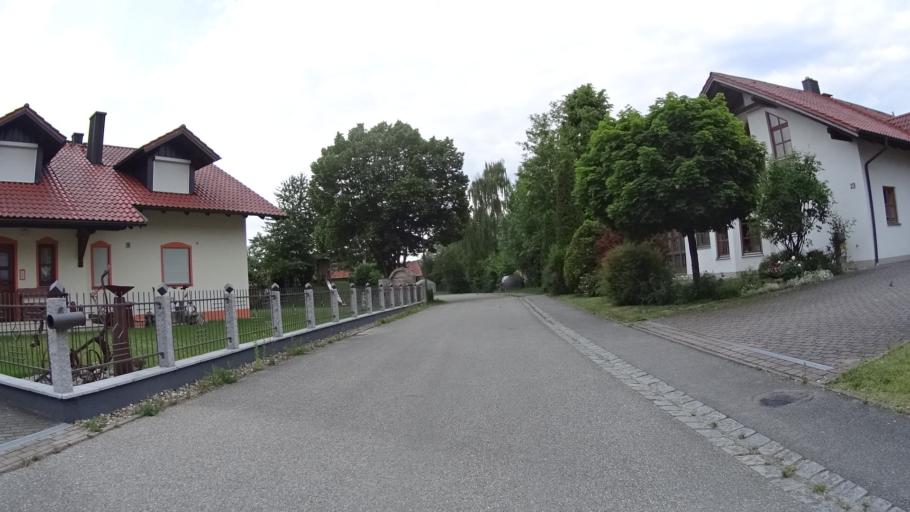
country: DE
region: Bavaria
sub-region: Lower Bavaria
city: Kirchroth
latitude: 48.9332
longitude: 12.5483
